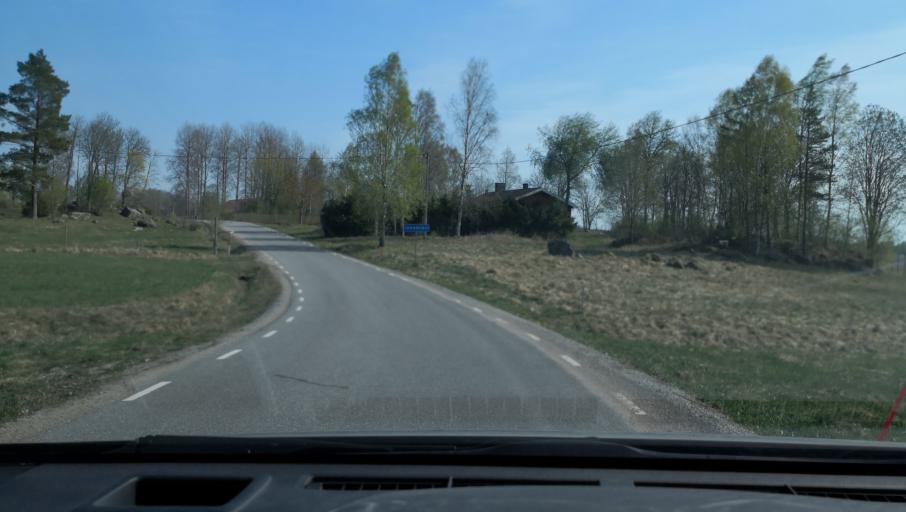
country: SE
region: Vaestmanland
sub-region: Sala Kommun
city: Sala
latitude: 60.0085
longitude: 16.6886
